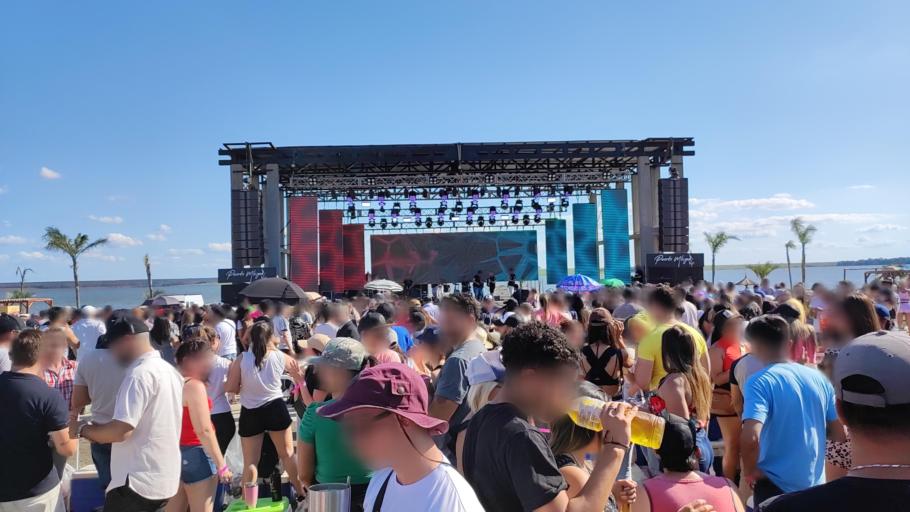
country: PY
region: Itapua
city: Carmen del Parana
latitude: -27.4199
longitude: -56.1770
